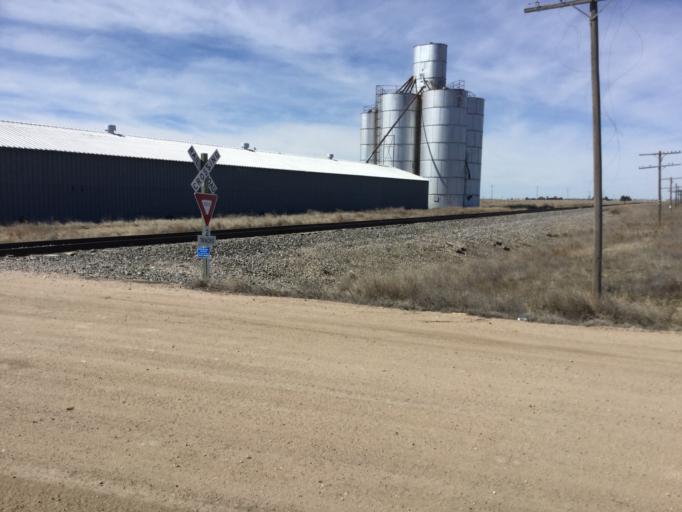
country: US
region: Kansas
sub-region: Greeley County
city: Tribune
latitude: 38.4549
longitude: -101.6783
